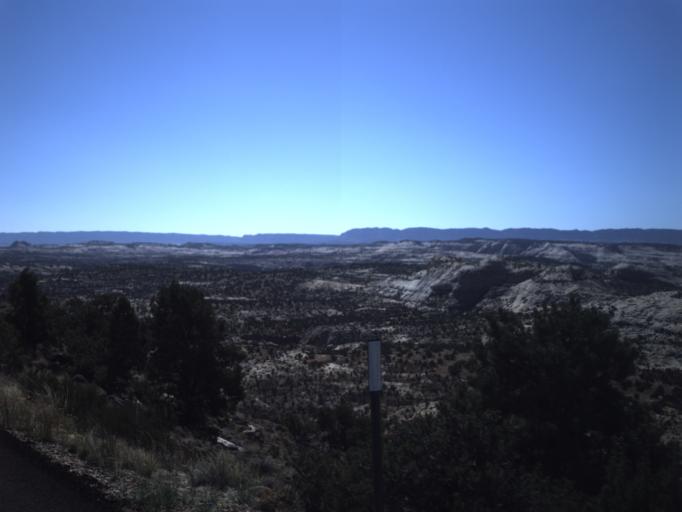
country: US
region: Utah
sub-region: Wayne County
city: Loa
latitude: 37.8370
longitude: -111.4195
